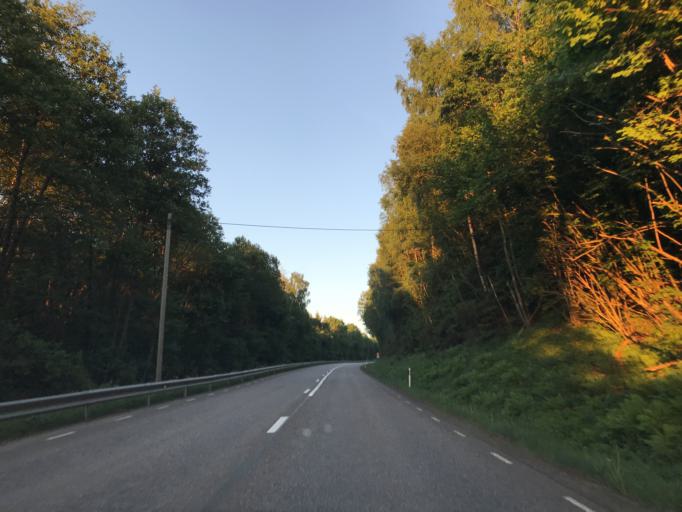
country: SE
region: Vaestra Goetaland
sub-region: Marks Kommun
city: Bua
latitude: 57.5185
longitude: 12.5523
